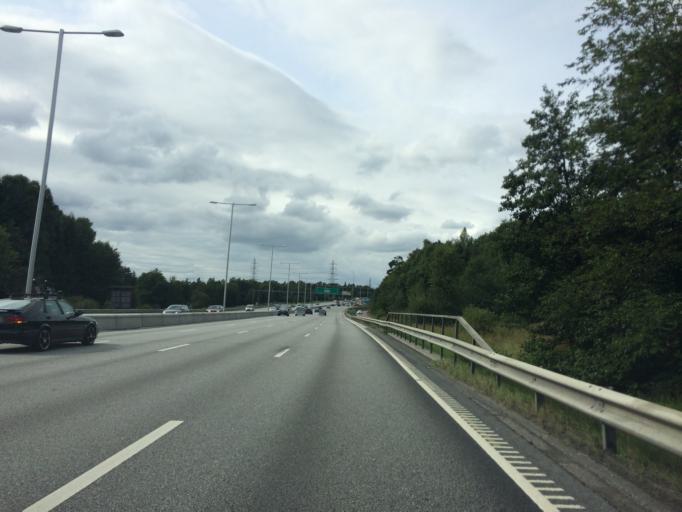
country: SE
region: Stockholm
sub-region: Solna Kommun
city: Rasunda
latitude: 59.3904
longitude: 17.9964
